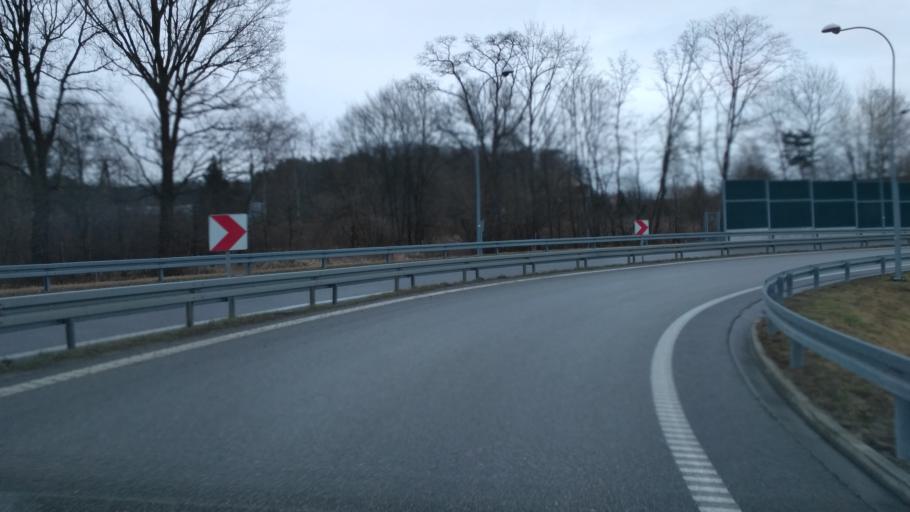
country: PL
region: Subcarpathian Voivodeship
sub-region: Powiat debicki
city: Brzeznica
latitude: 50.0805
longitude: 21.4709
